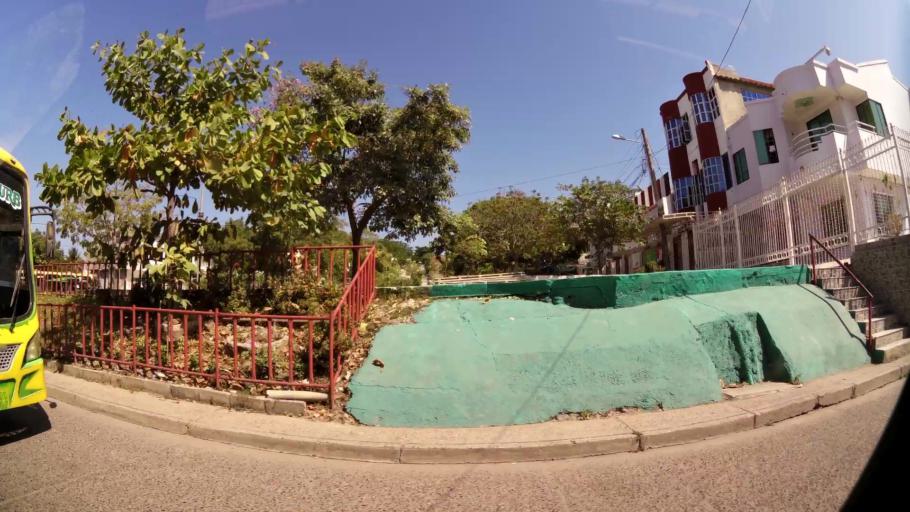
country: CO
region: Bolivar
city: Cartagena
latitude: 10.3894
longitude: -75.5106
